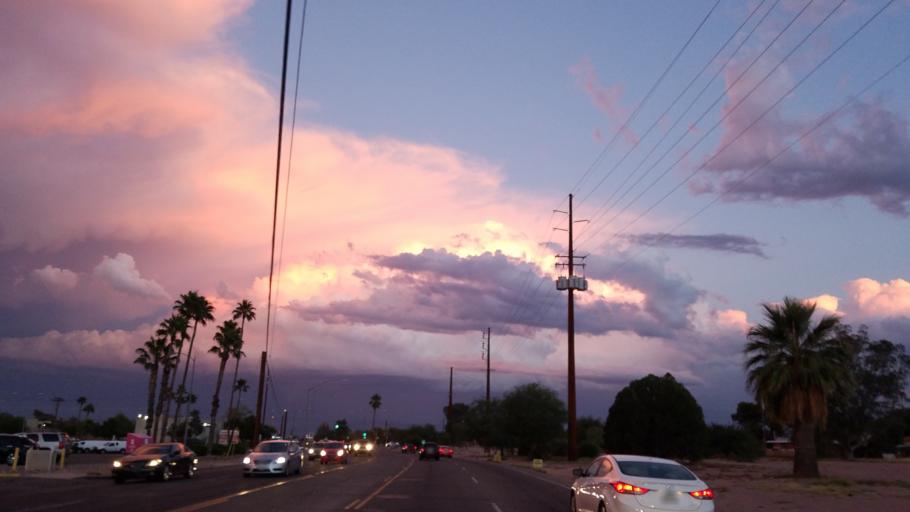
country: US
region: Arizona
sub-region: Pima County
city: Tucson
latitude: 32.2502
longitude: -110.9593
